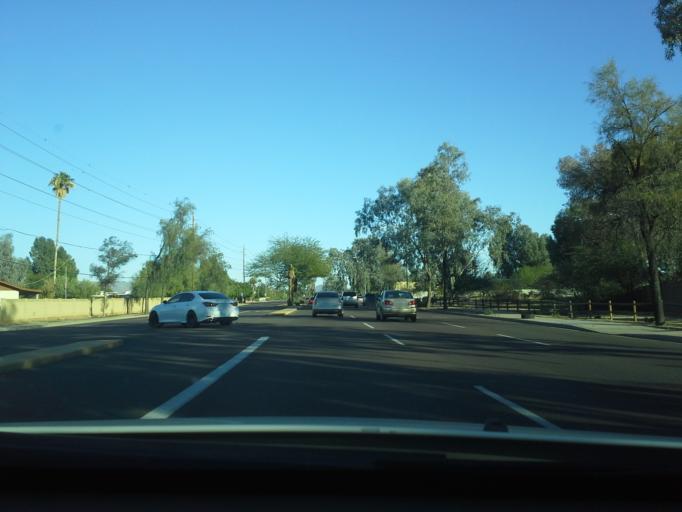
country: US
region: Arizona
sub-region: Maricopa County
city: Paradise Valley
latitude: 33.5824
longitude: -111.9536
